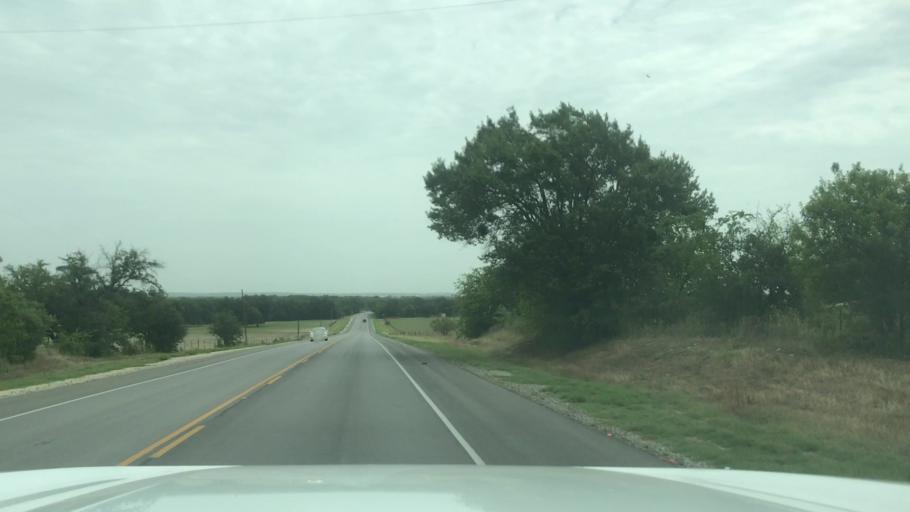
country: US
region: Texas
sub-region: Erath County
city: Dublin
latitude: 32.0866
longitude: -98.3115
